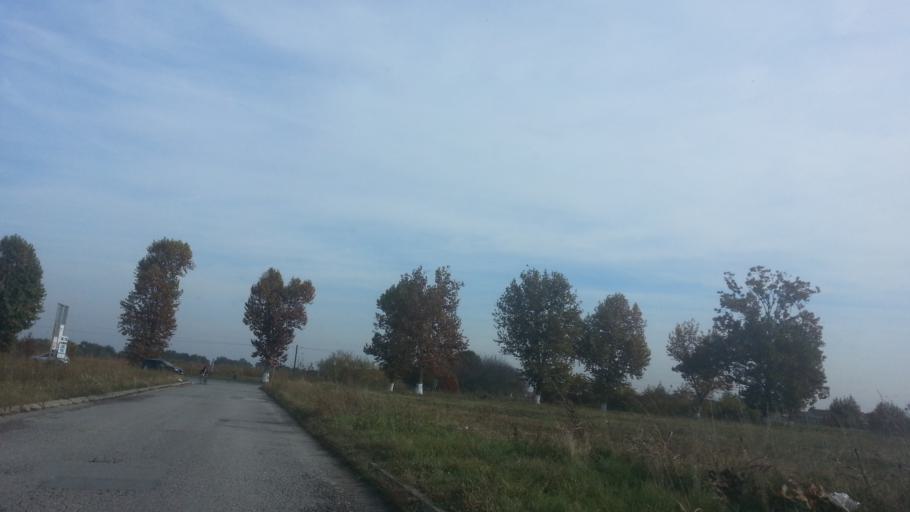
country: RS
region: Autonomna Pokrajina Vojvodina
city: Nova Pazova
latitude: 44.9544
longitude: 20.2026
